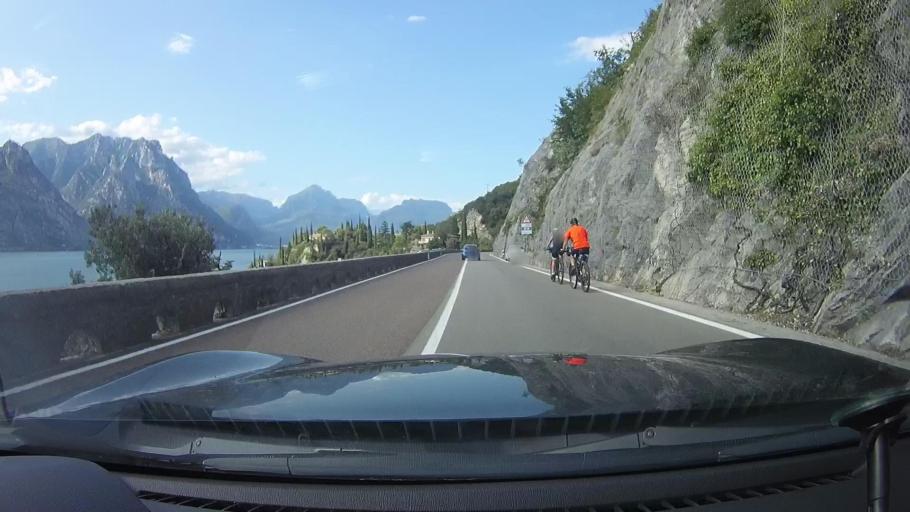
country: IT
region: Trentino-Alto Adige
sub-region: Provincia di Trento
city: Torbole sul Garda
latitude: 45.8323
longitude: 10.8598
